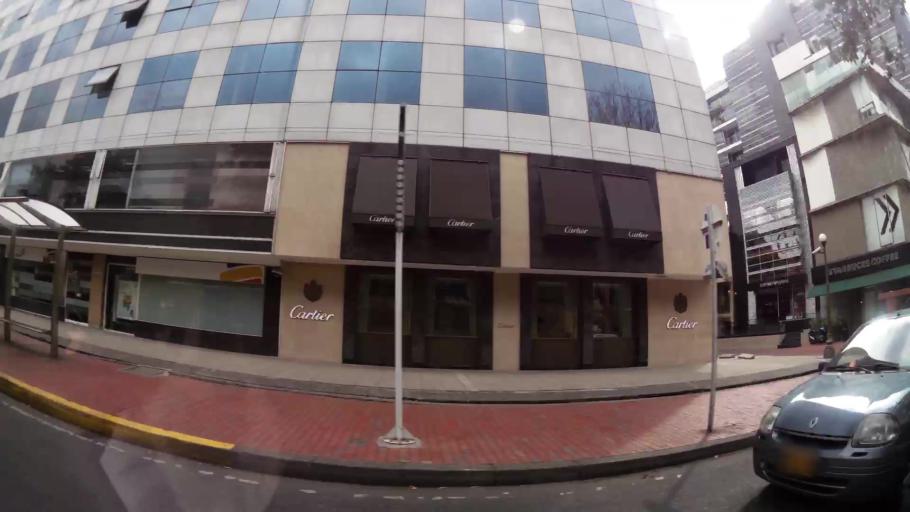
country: CO
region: Bogota D.C.
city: Barrio San Luis
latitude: 4.6673
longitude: -74.0526
